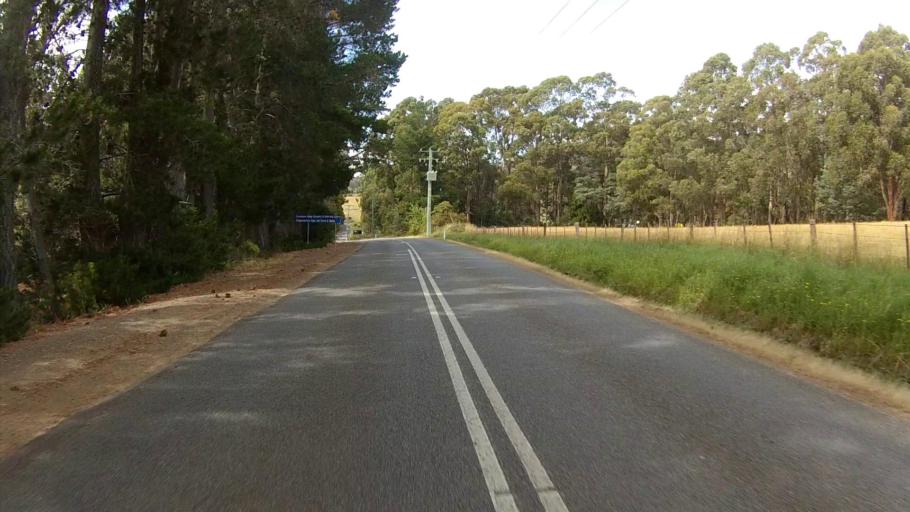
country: AU
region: Tasmania
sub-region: Kingborough
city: Kettering
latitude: -43.1794
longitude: 147.2377
